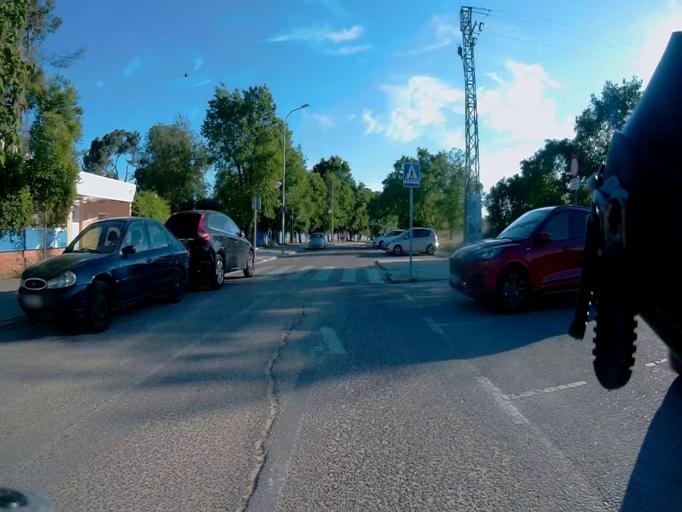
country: ES
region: Madrid
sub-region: Provincia de Madrid
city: Alcorcon
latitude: 40.3373
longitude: -3.8441
